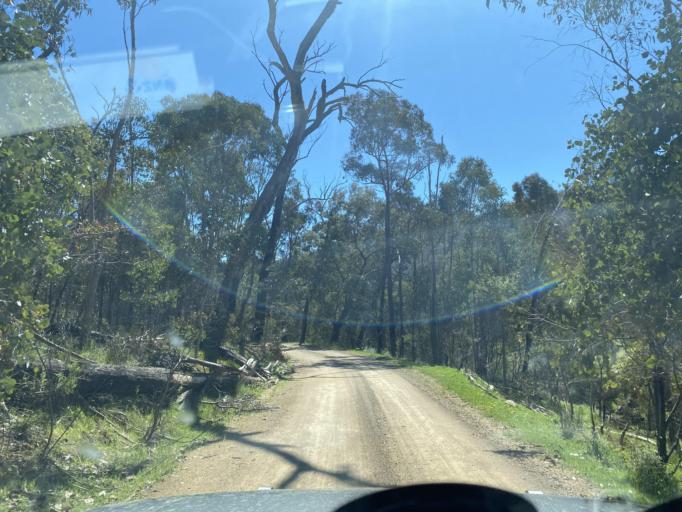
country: AU
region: Victoria
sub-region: Benalla
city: Benalla
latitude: -36.7043
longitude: 146.1782
